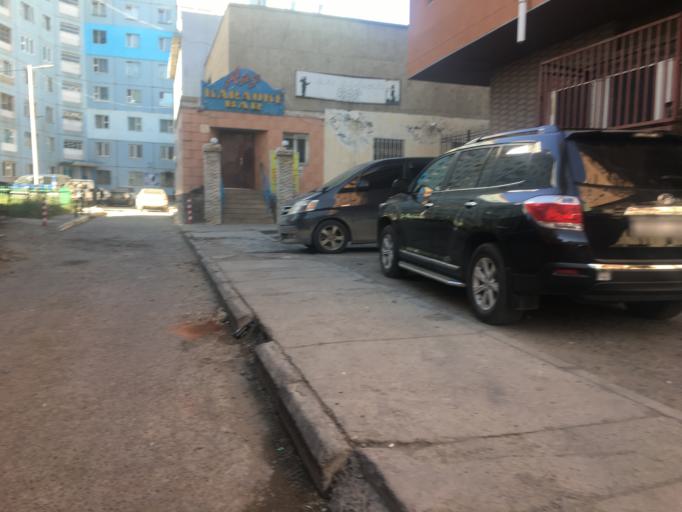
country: MN
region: Ulaanbaatar
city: Ulaanbaatar
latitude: 47.9225
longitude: 106.8861
